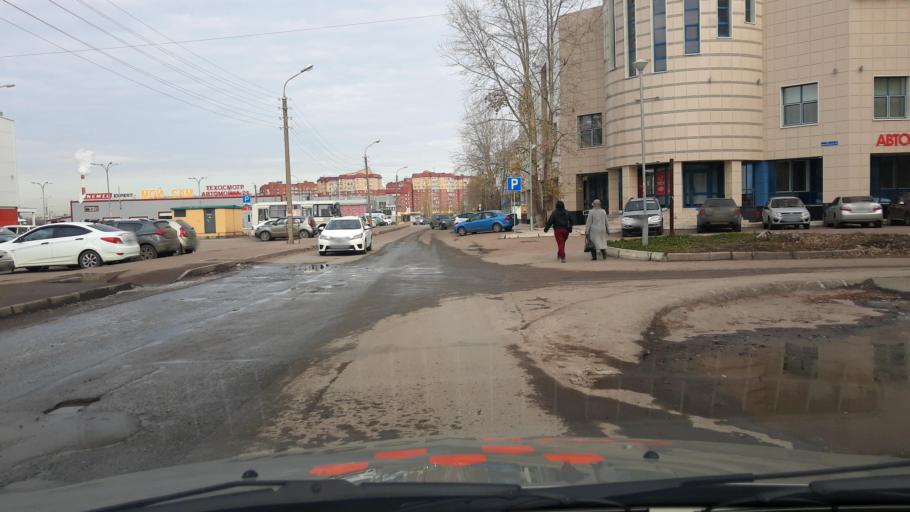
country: RU
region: Bashkortostan
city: Ufa
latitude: 54.7709
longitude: 56.0627
